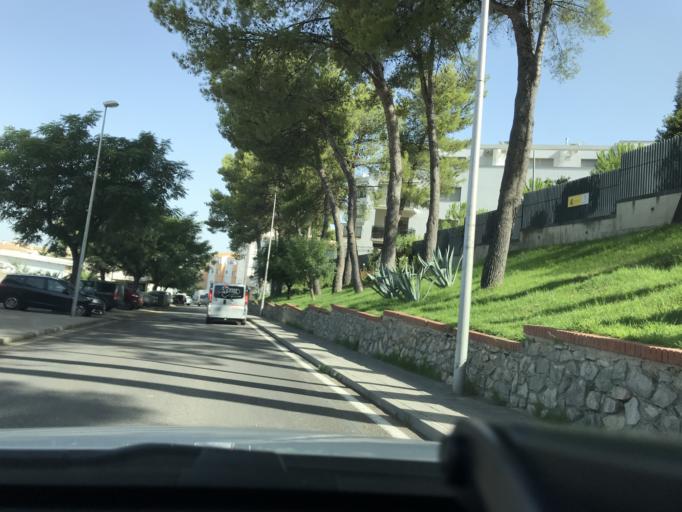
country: ES
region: Andalusia
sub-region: Provincia de Jaen
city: Cazorla
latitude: 37.9176
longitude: -3.0049
